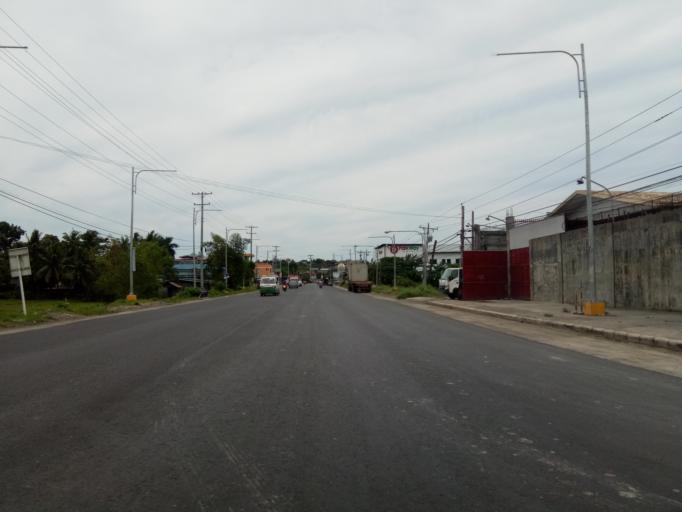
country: PH
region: Caraga
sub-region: Province of Surigao del Norte
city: Rizal
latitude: 9.7703
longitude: 125.4835
